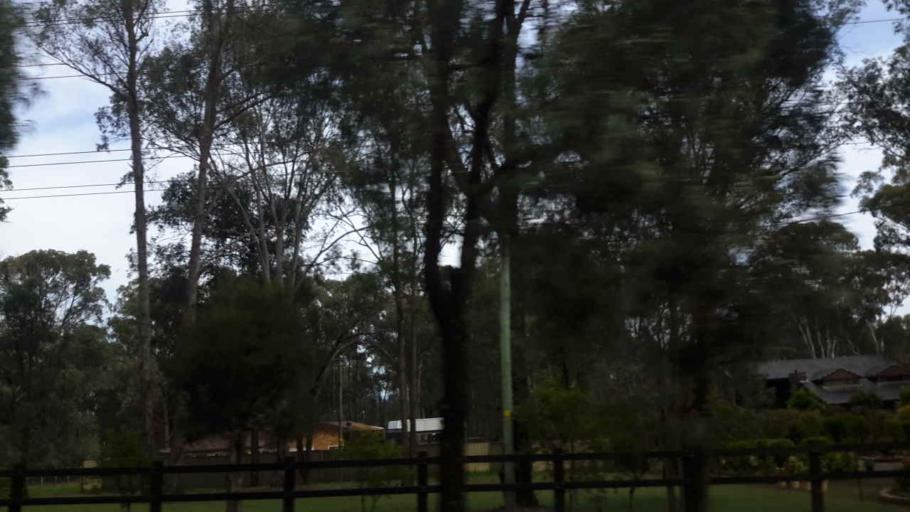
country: AU
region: New South Wales
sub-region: Hawkesbury
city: South Windsor
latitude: -33.6465
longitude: 150.7805
